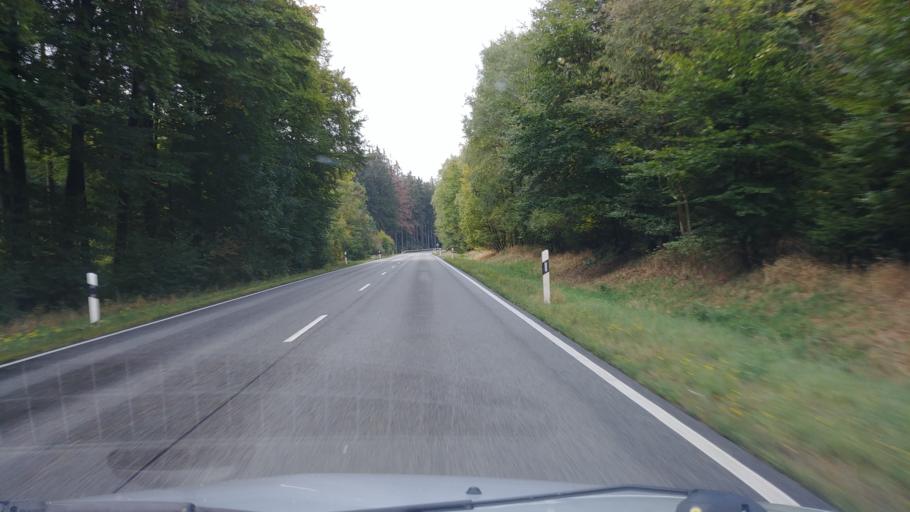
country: DE
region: Rheinland-Pfalz
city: Hochscheid
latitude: 49.8680
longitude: 7.1957
